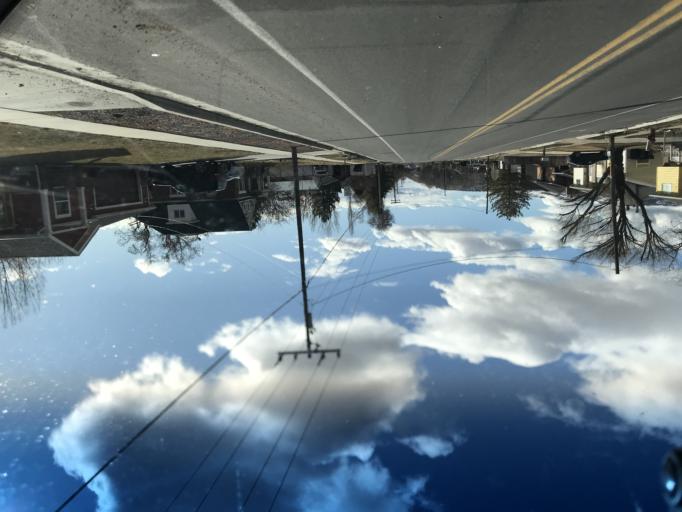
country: US
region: Utah
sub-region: Davis County
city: Woods Cross
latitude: 40.8744
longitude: -111.9118
